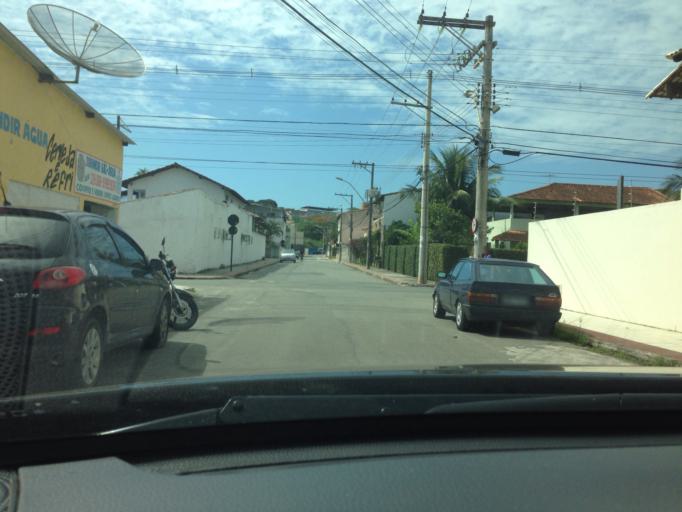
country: BR
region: Espirito Santo
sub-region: Guarapari
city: Guarapari
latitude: -20.6721
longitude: -40.5058
